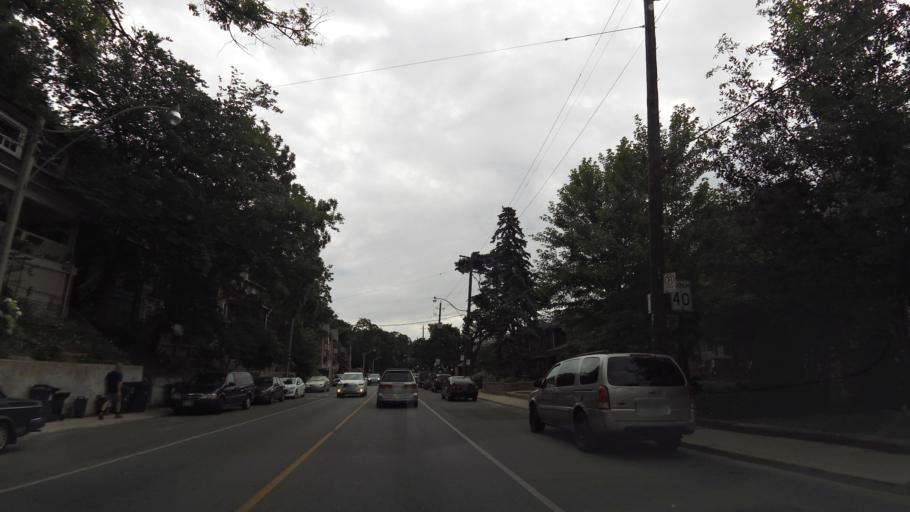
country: CA
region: Ontario
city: Toronto
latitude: 43.6758
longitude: -79.4223
